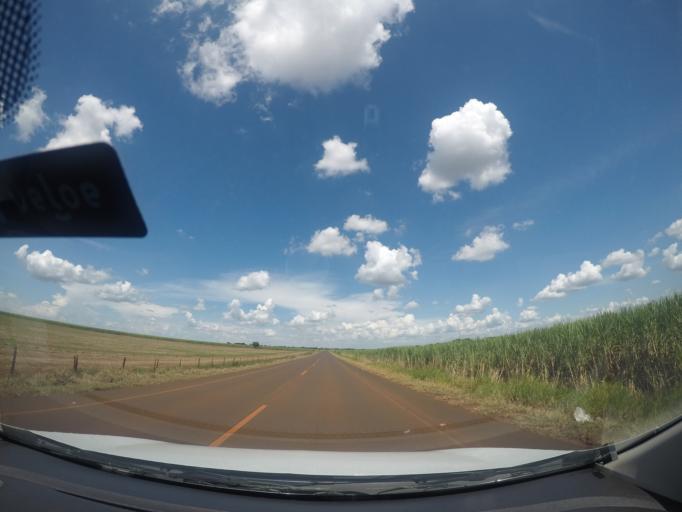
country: BR
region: Minas Gerais
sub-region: Conceicao Das Alagoas
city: Conceicao das Alagoas
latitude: -19.9243
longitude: -48.6710
